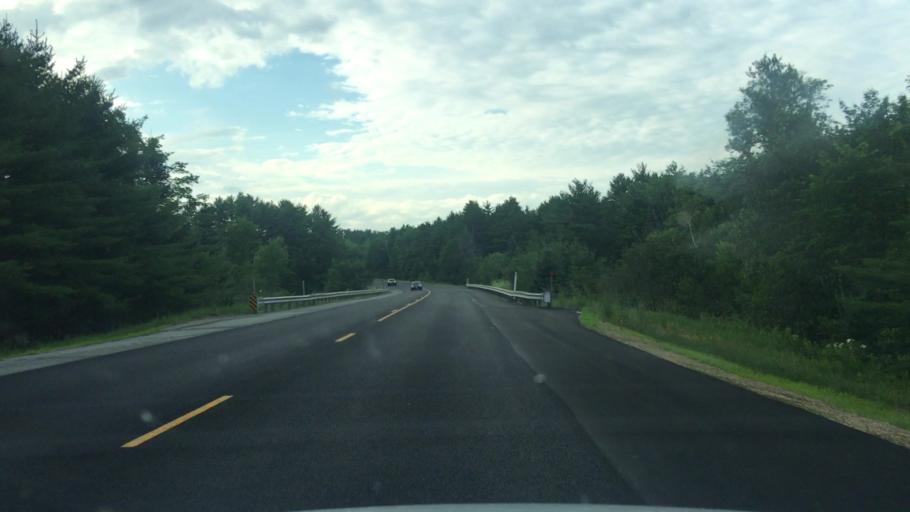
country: US
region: Maine
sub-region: Waldo County
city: Palermo
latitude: 44.4066
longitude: -69.4800
